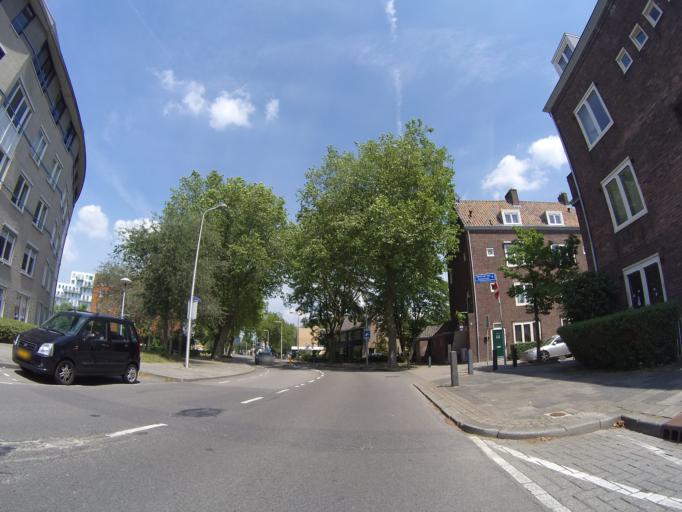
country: NL
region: Utrecht
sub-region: Gemeente Utrecht
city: Utrecht
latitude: 52.1011
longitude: 5.1357
